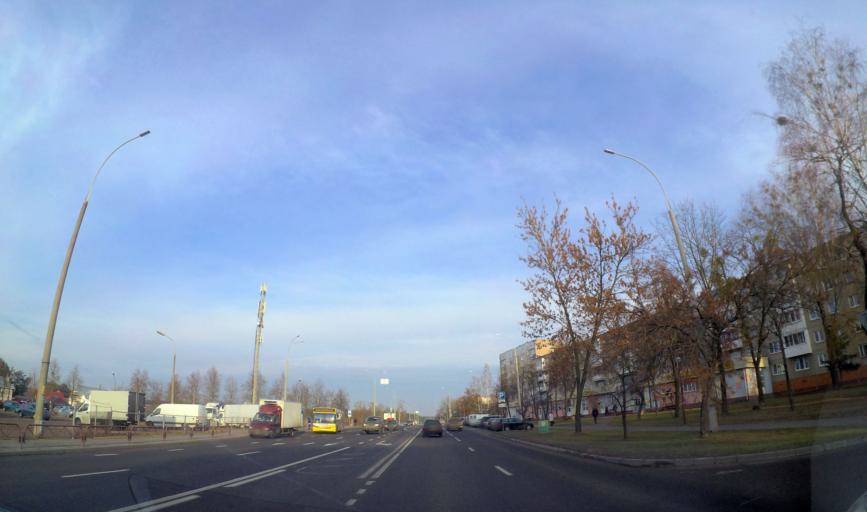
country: BY
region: Grodnenskaya
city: Hrodna
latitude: 53.6686
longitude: 23.7899
